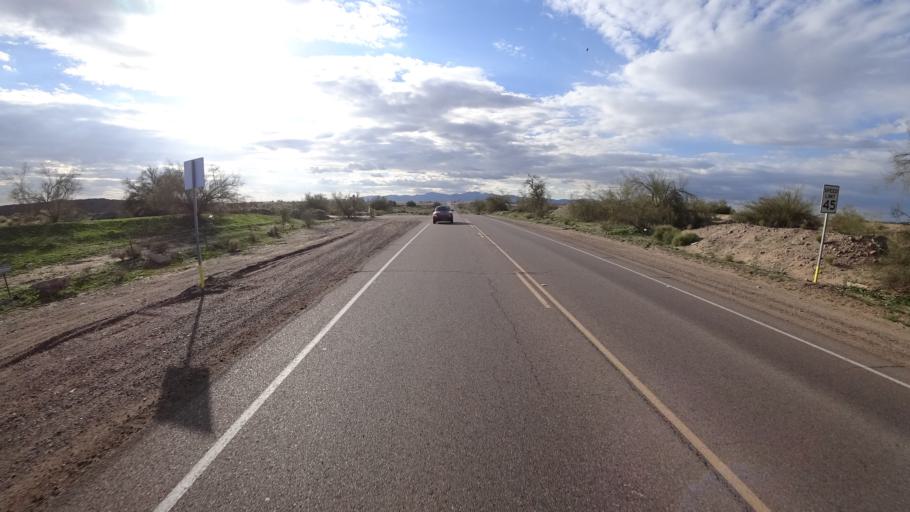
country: US
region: Arizona
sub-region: Maricopa County
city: Youngtown
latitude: 33.5509
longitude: -112.3145
